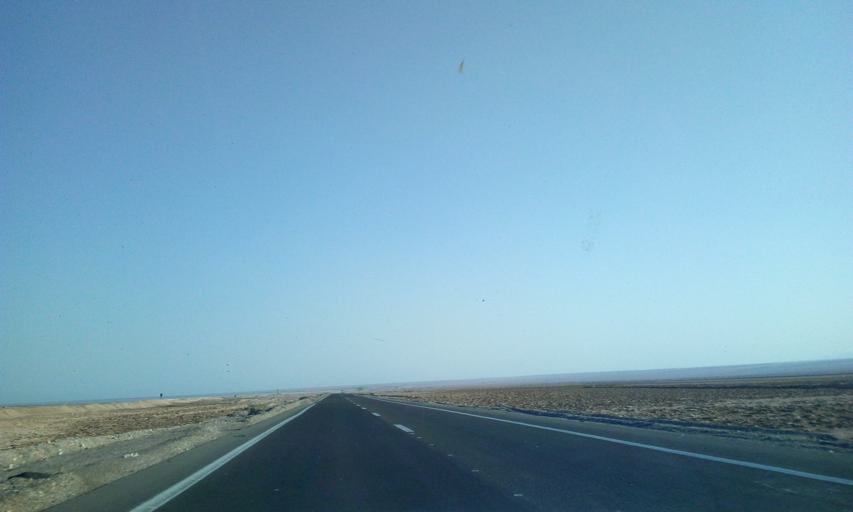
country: EG
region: South Sinai
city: Tor
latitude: 28.6160
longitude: 32.8608
